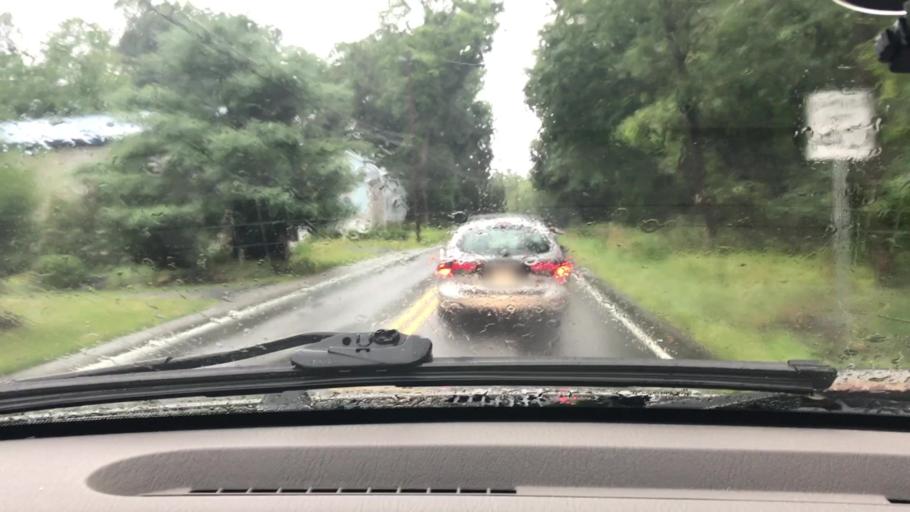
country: US
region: Pennsylvania
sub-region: Lancaster County
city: Elizabethtown
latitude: 40.1472
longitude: -76.6237
